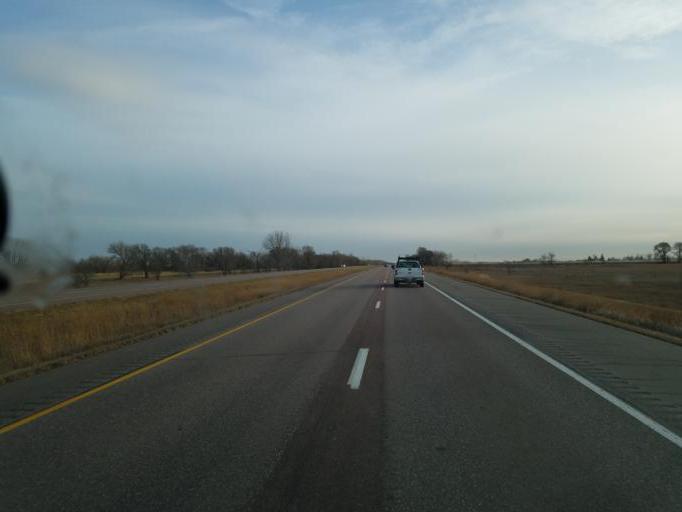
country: US
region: Nebraska
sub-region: Thurston County
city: Macy
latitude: 42.1531
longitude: -96.2210
